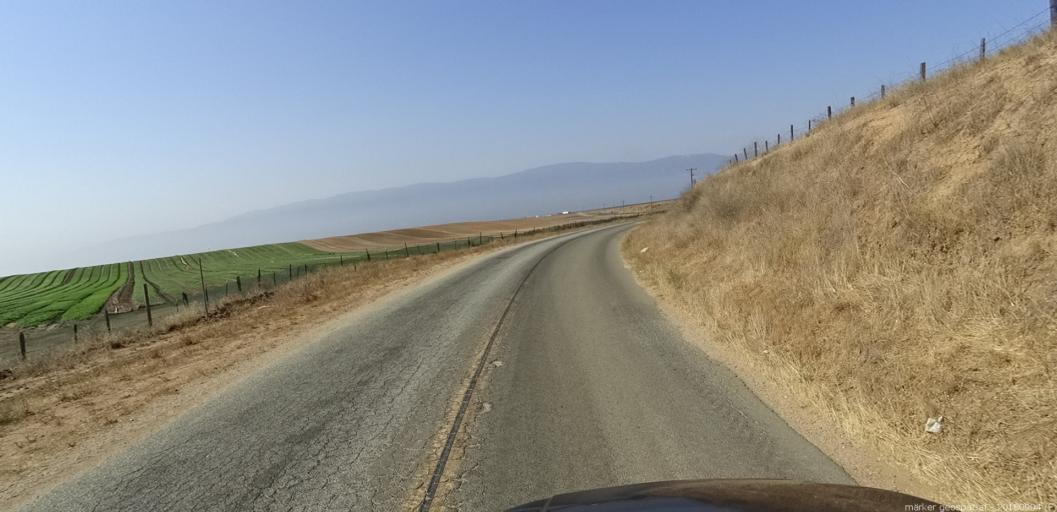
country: US
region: California
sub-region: Monterey County
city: Gonzales
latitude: 36.5099
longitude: -121.3658
